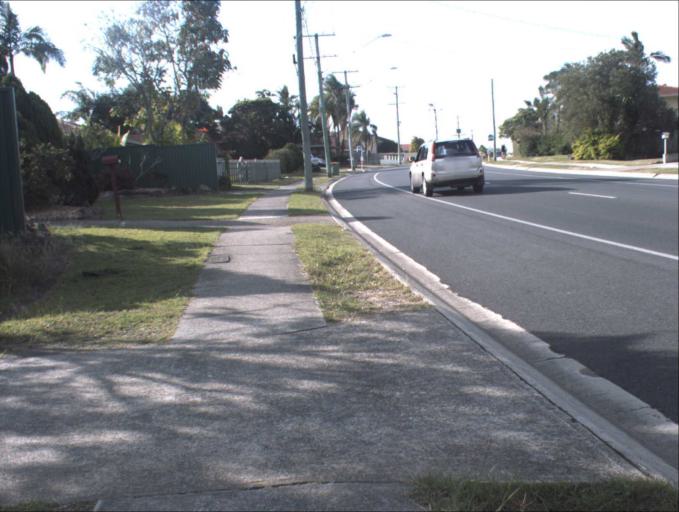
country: AU
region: Queensland
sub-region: Logan
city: Park Ridge South
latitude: -27.6723
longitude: 153.0371
